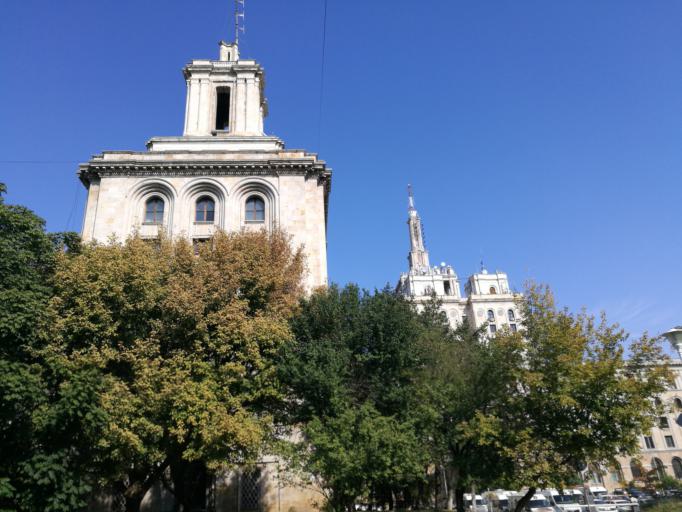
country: RO
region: Bucuresti
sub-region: Municipiul Bucuresti
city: Bucuresti
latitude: 44.4808
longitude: 26.0690
